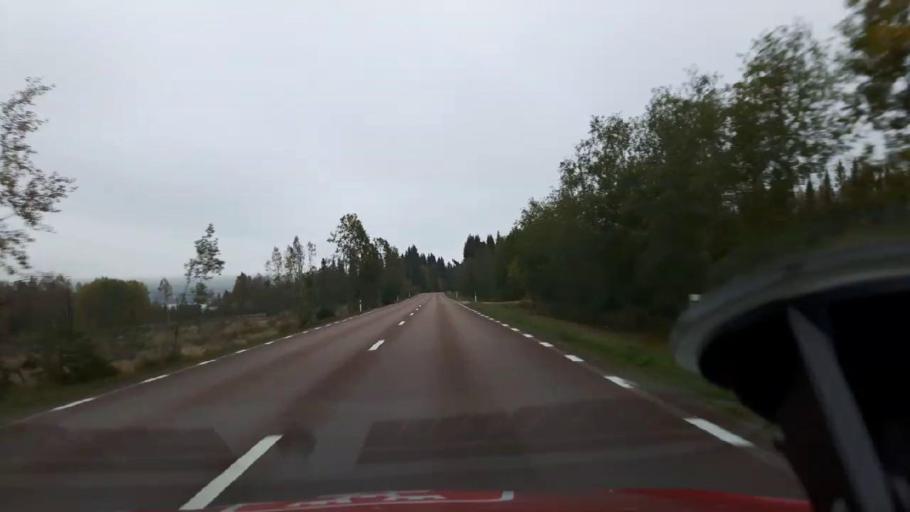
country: SE
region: Jaemtland
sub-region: Bergs Kommun
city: Hoverberg
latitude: 62.5791
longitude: 14.4454
